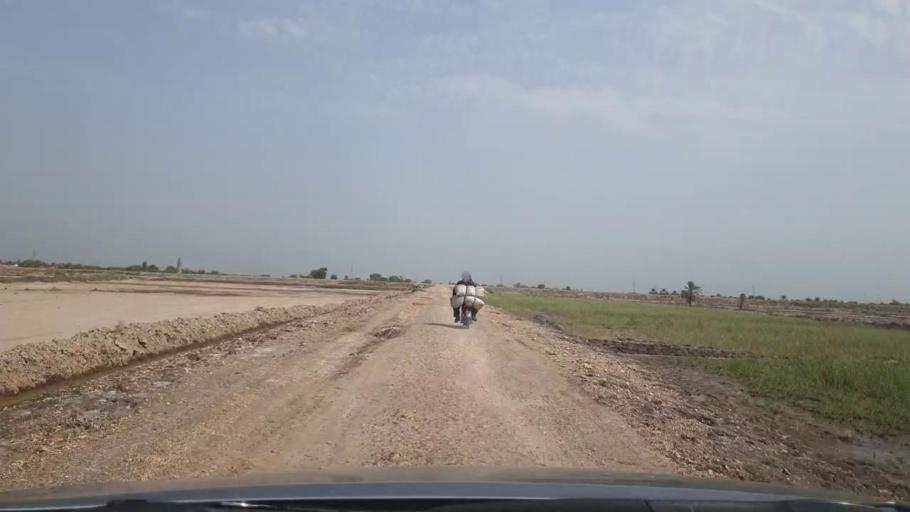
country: PK
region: Sindh
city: Rohri
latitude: 27.6767
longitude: 69.0259
